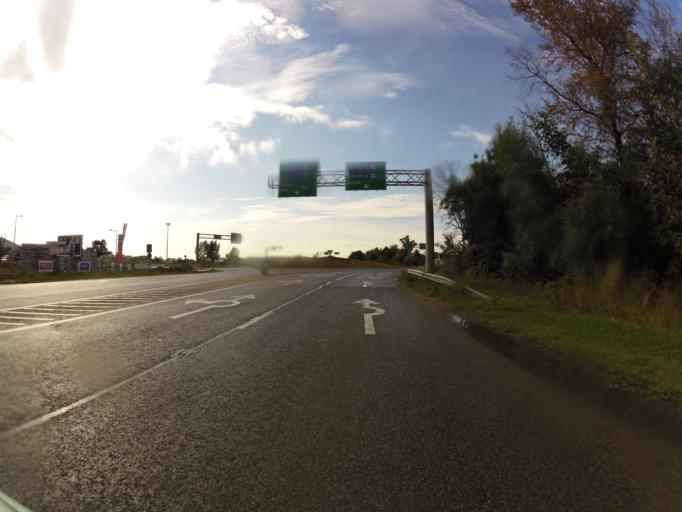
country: HU
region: Csongrad
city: Szeged
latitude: 46.2817
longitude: 20.0932
